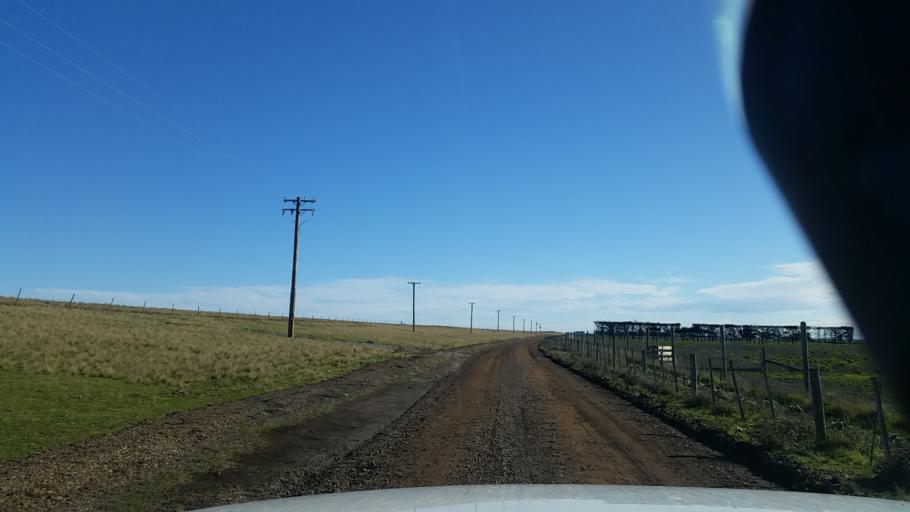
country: NZ
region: Canterbury
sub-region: Selwyn District
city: Lincoln
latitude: -43.8119
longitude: 172.6599
